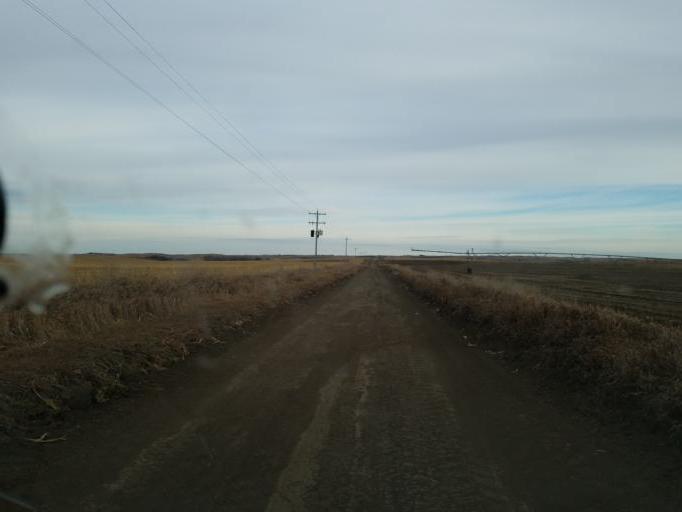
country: US
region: Nebraska
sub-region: Knox County
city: Bloomfield
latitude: 42.5280
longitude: -97.7204
